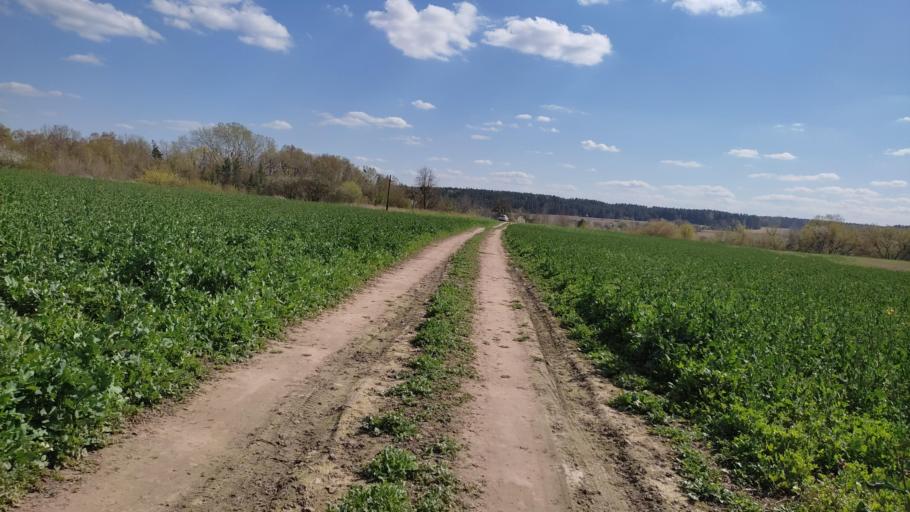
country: BY
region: Grodnenskaya
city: Hrodna
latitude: 53.6557
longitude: 23.9057
